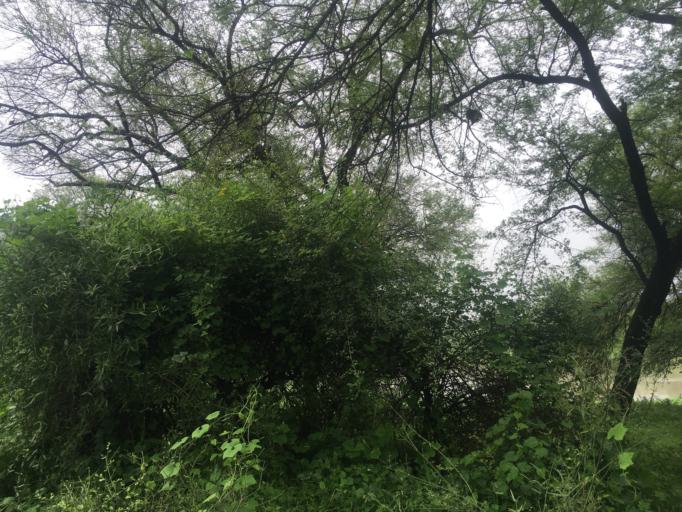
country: IN
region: Gujarat
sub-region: Mahesana
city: Kadi
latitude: 23.1617
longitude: 72.3793
